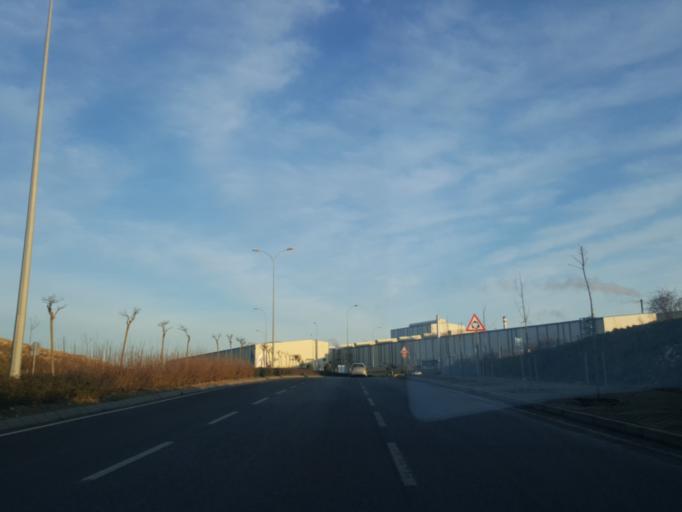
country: TR
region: Kocaeli
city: Tavsanli
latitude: 40.8294
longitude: 29.5591
